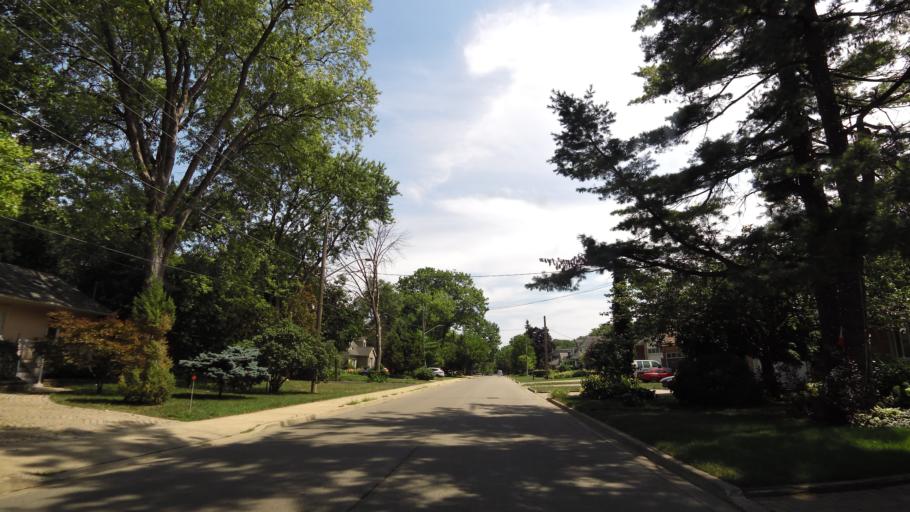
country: CA
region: Ontario
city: Mississauga
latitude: 43.5755
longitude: -79.5884
